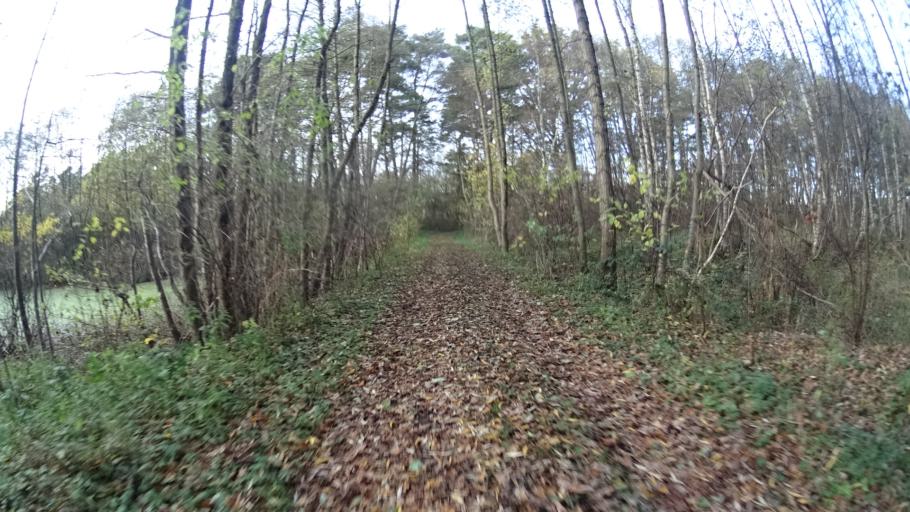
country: DE
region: Lower Saxony
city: Wendisch Evern
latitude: 53.2180
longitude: 10.4470
